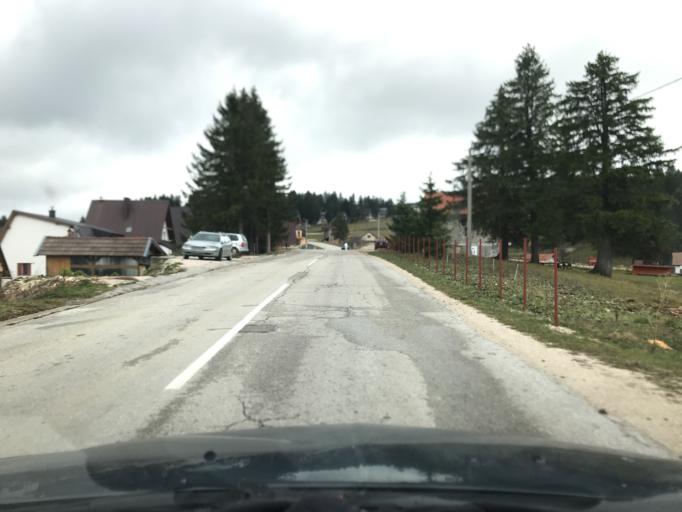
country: BA
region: Federation of Bosnia and Herzegovina
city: Turbe
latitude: 44.3141
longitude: 17.5623
